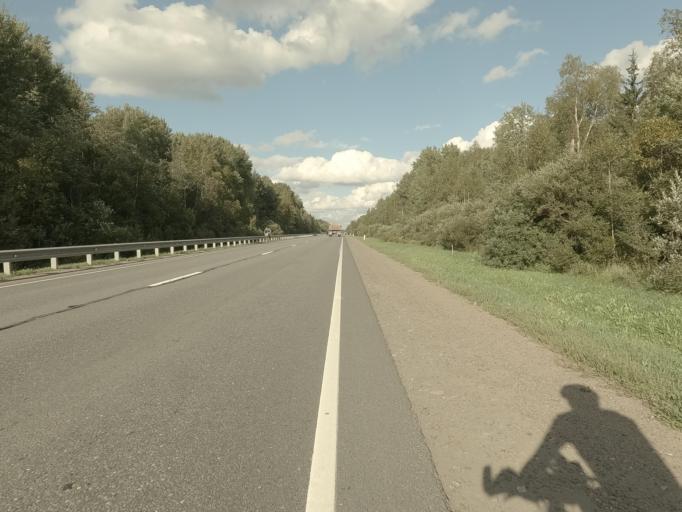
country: RU
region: Leningrad
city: Nikol'skoye
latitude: 59.6506
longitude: 30.8513
